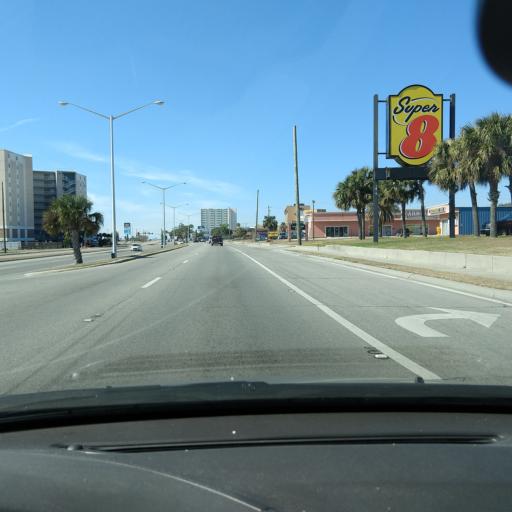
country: US
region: Mississippi
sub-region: Harrison County
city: Biloxi
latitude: 30.3936
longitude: -88.9497
